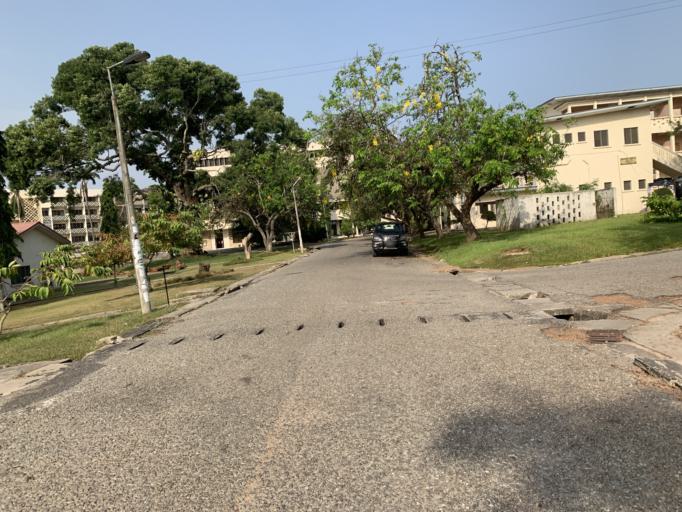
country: GH
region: Central
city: Winneba
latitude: 5.3382
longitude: -0.6259
